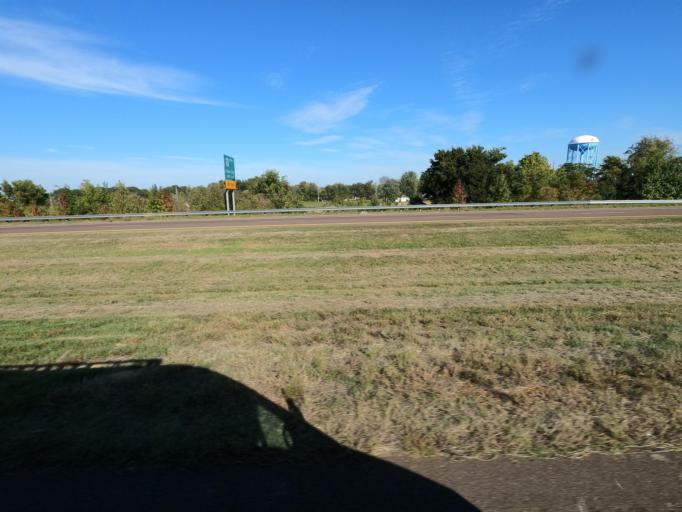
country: US
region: Tennessee
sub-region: Dyer County
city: Dyersburg
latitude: 36.0676
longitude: -89.3445
